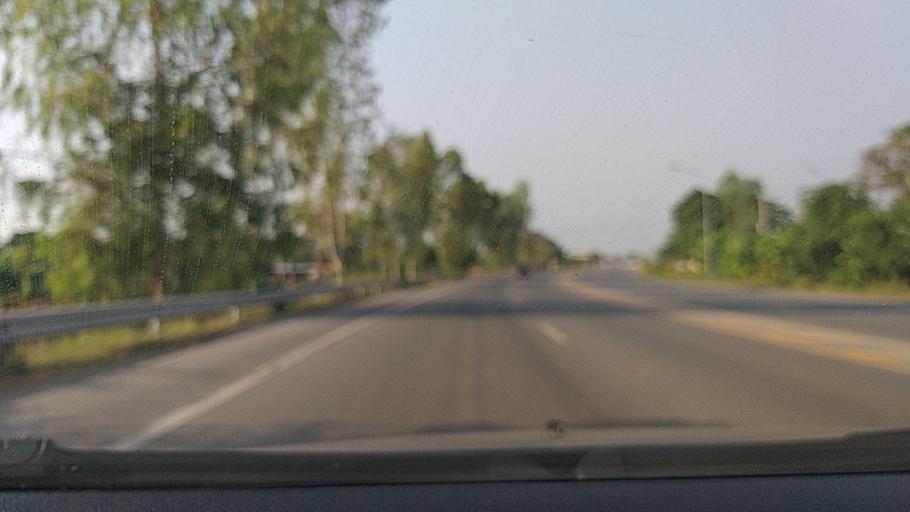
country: TH
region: Sing Buri
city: Sing Buri
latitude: 14.8631
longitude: 100.4052
